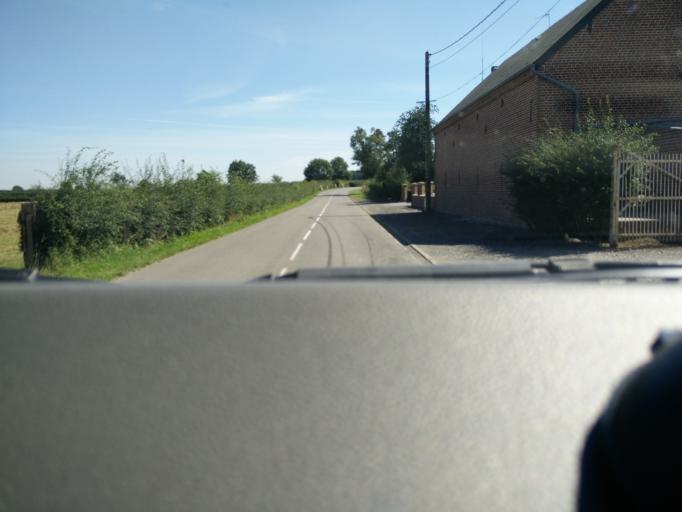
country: FR
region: Nord-Pas-de-Calais
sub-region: Departement du Nord
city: Bachant
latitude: 50.1842
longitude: 3.9009
